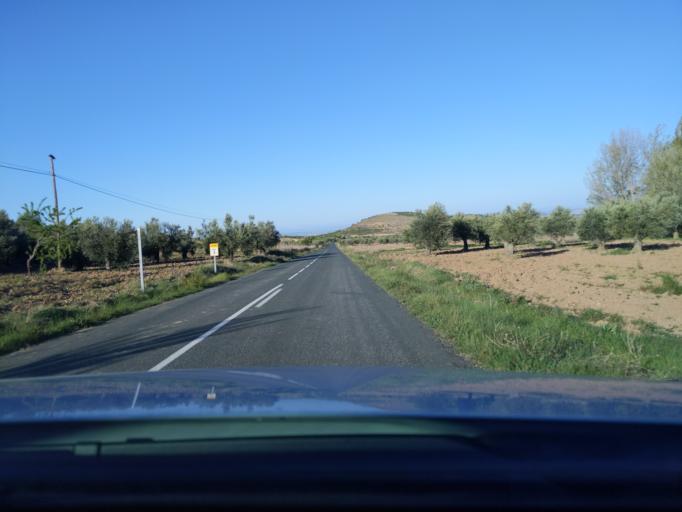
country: ES
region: La Rioja
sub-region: Provincia de La Rioja
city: Bergasa
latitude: 42.2646
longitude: -2.1065
